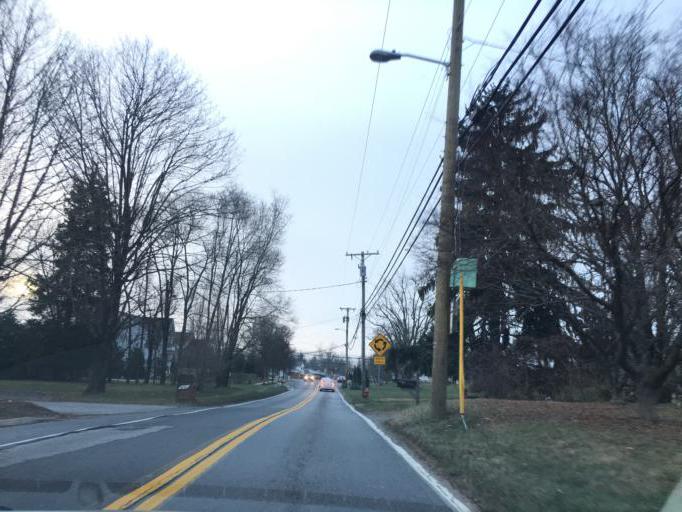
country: US
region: Maryland
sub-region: Baltimore County
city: Randallstown
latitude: 39.3600
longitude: -76.7907
